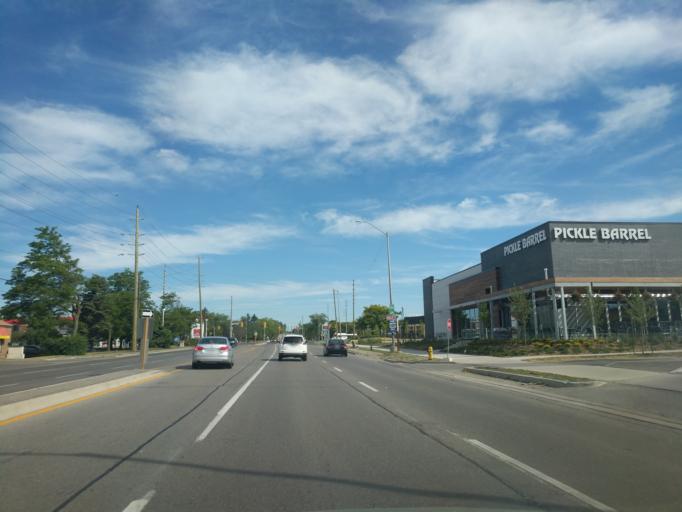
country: CA
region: Ontario
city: Ajax
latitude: 43.8340
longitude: -79.0897
